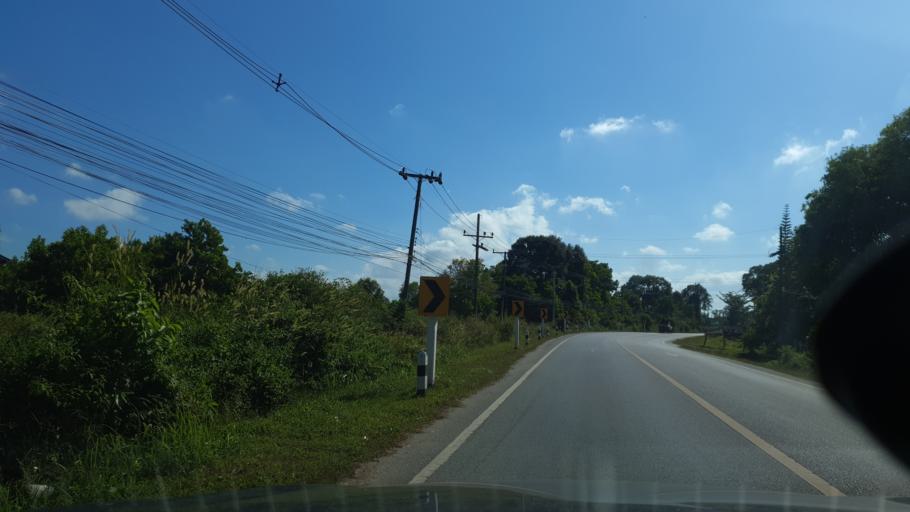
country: TH
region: Krabi
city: Krabi
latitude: 8.0293
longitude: 98.8685
